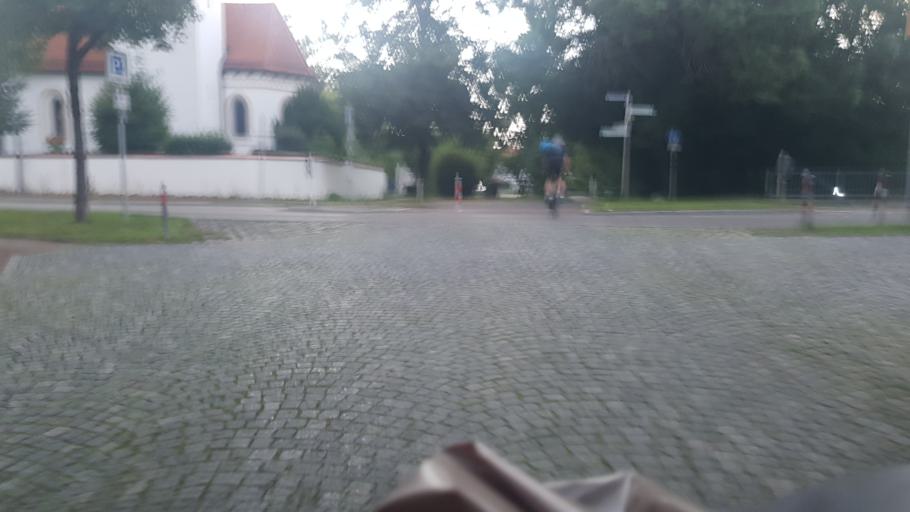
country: DE
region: Bavaria
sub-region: Upper Bavaria
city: Grafelfing
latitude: 48.1158
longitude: 11.4361
